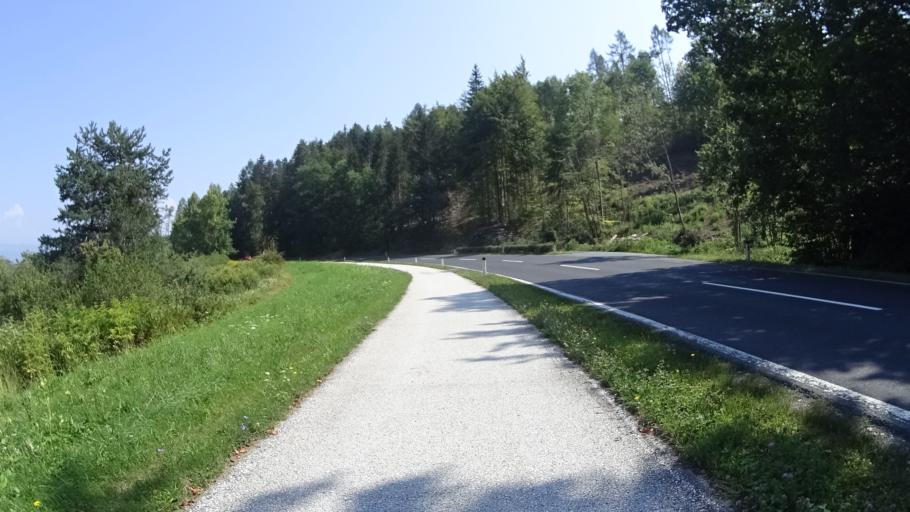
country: AT
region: Carinthia
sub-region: Politischer Bezirk Volkermarkt
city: Sittersdorf
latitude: 46.5587
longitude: 14.6224
